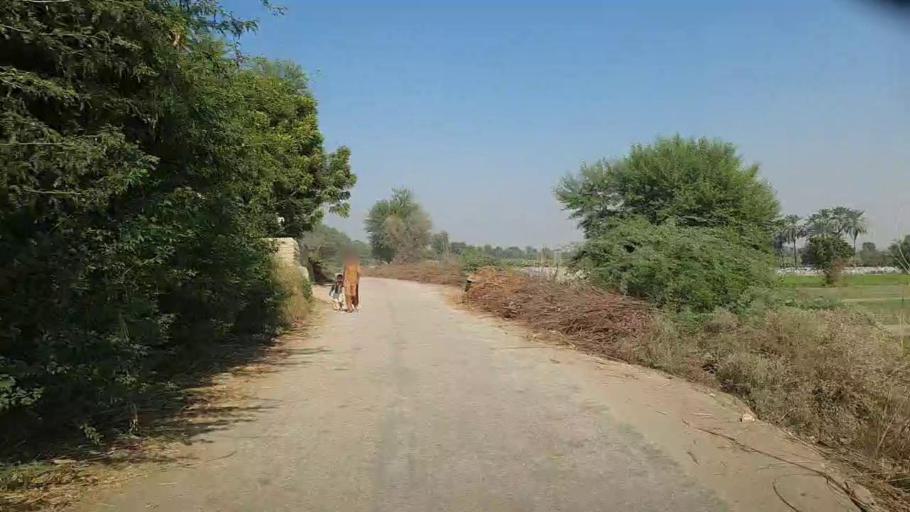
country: PK
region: Sindh
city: Bozdar
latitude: 27.2004
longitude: 68.6651
